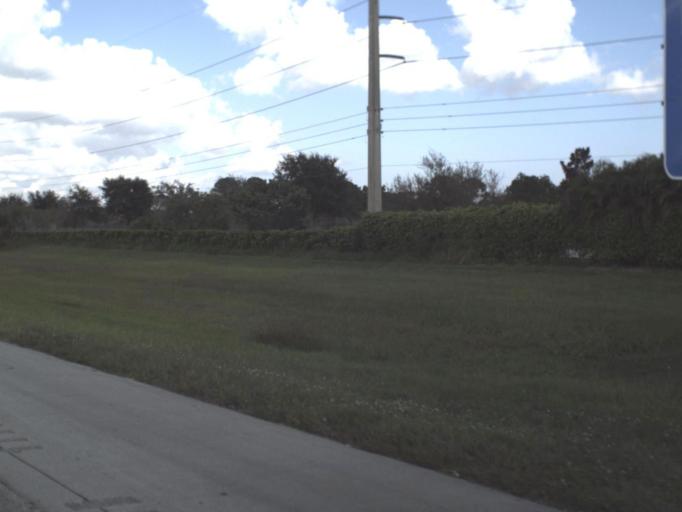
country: US
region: Florida
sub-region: Martin County
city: Palm City
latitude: 27.1845
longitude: -80.3202
